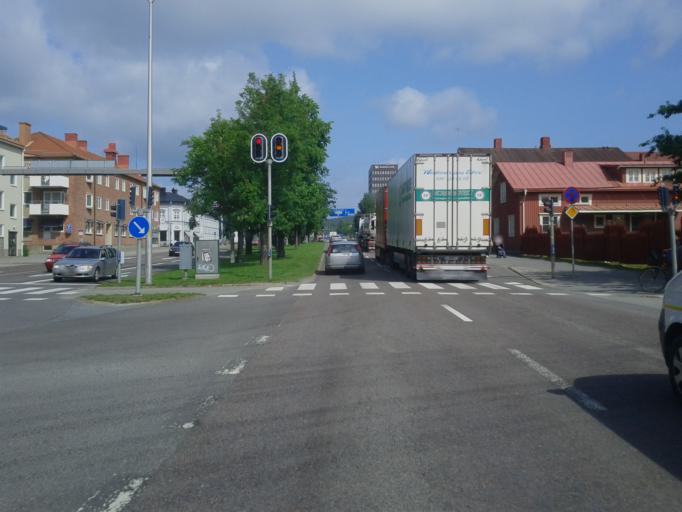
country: SE
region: Vaesterbotten
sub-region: Skelleftea Kommun
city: Skelleftea
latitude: 64.7492
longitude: 20.9605
